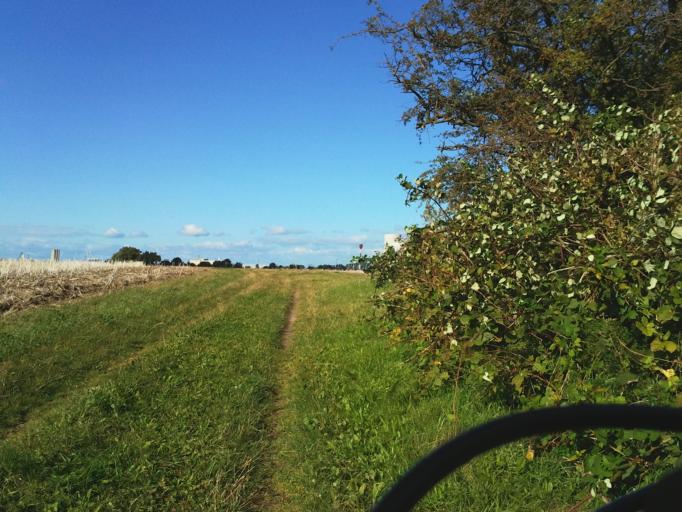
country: DE
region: Mecklenburg-Vorpommern
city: Dierkow-West
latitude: 54.1235
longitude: 12.1146
